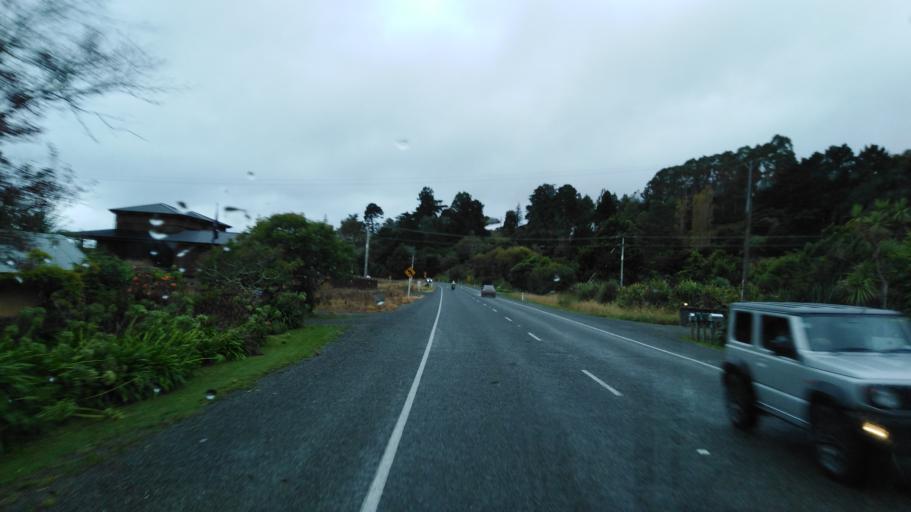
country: NZ
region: Nelson
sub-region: Nelson City
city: Nelson
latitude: -41.2200
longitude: 173.3290
